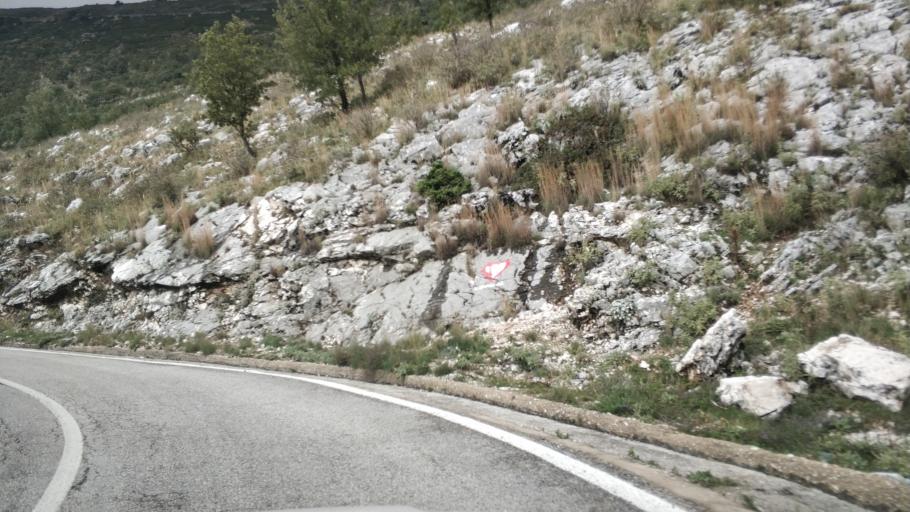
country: AL
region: Vlore
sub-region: Rrethi i Vlores
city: Vranisht
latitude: 40.1859
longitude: 19.6101
